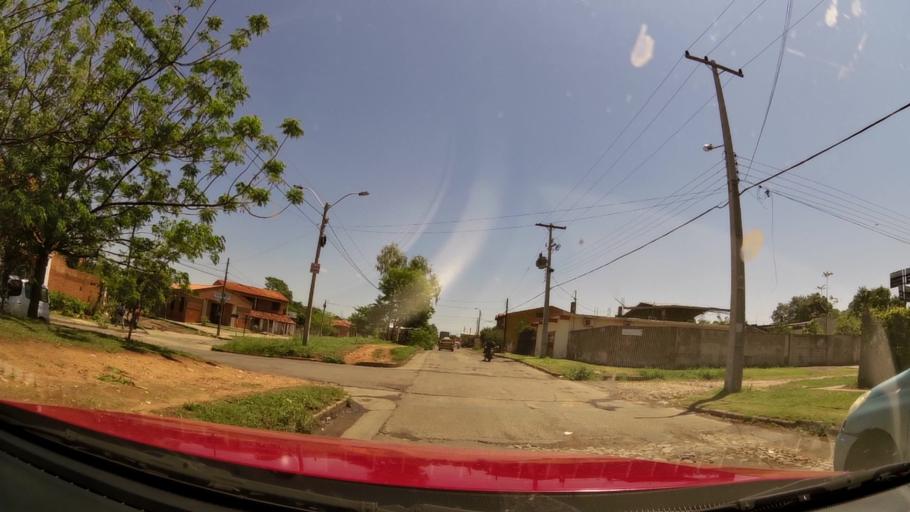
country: PY
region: Central
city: Colonia Mariano Roque Alonso
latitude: -25.2342
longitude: -57.5455
